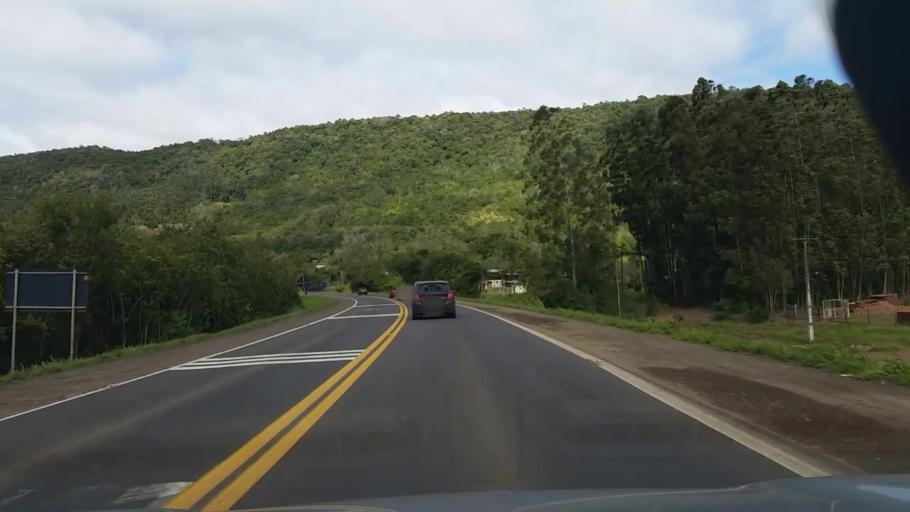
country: BR
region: Rio Grande do Sul
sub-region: Arroio Do Meio
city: Arroio do Meio
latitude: -29.3293
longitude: -52.1016
